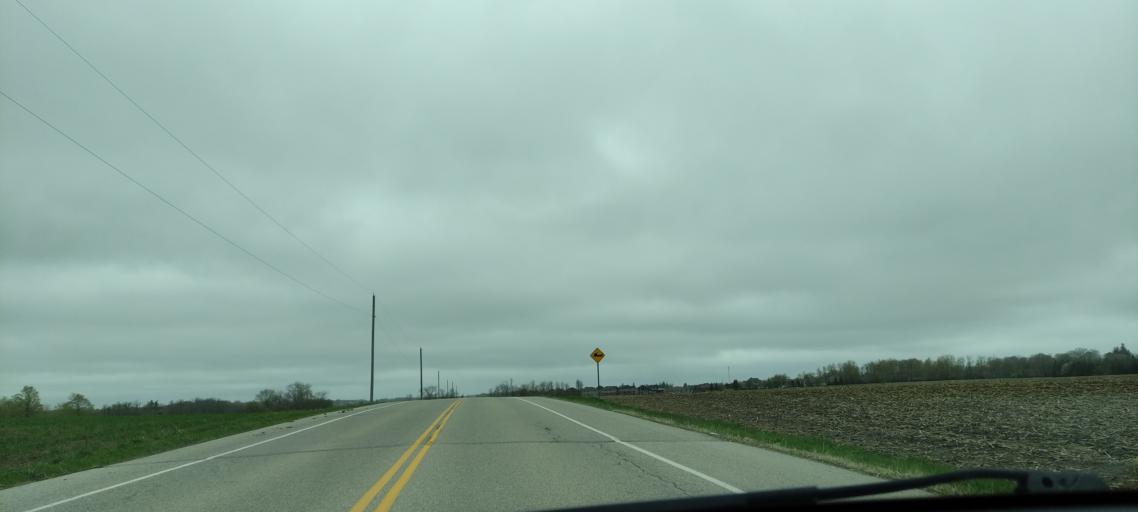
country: CA
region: Ontario
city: Waterloo
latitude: 43.4714
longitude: -80.7433
